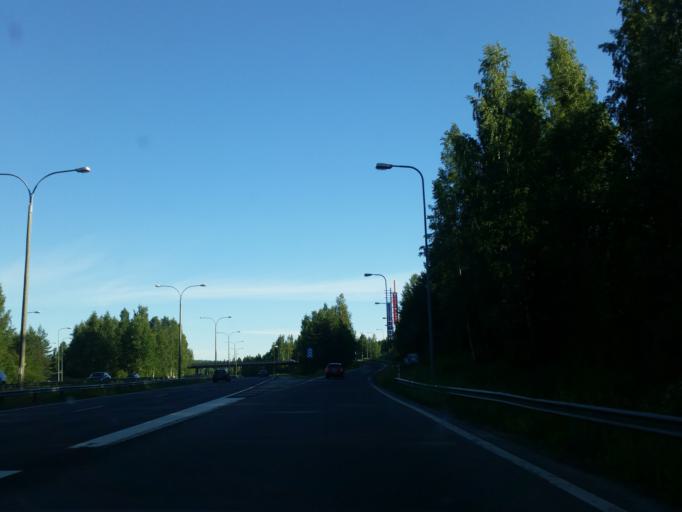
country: FI
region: Northern Savo
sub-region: Kuopio
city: Kuopio
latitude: 62.8651
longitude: 27.6180
